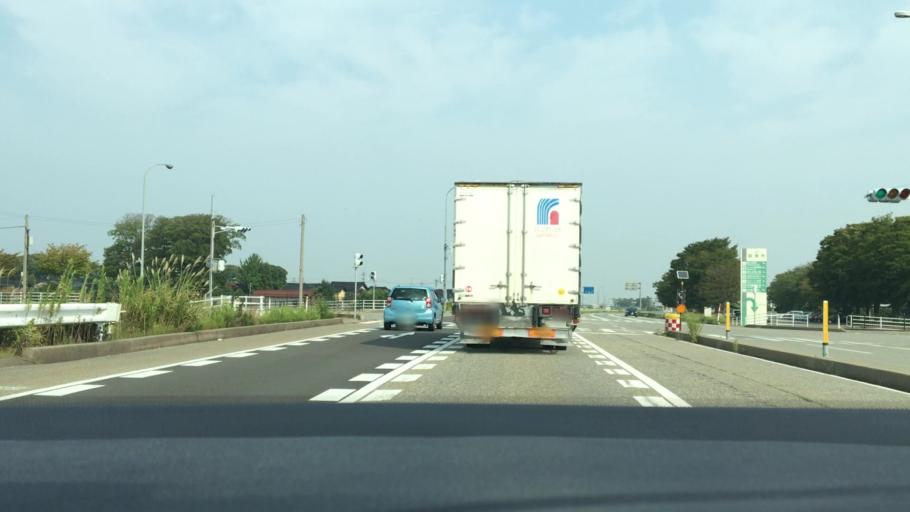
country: JP
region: Ishikawa
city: Matsuto
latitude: 36.5050
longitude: 136.5955
